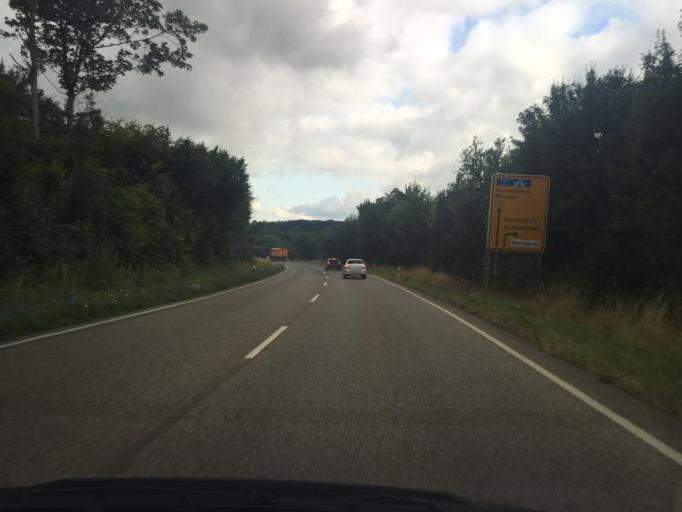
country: DE
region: Baden-Wuerttemberg
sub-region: Karlsruhe Region
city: Bruchsal
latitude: 49.1081
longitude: 8.6374
